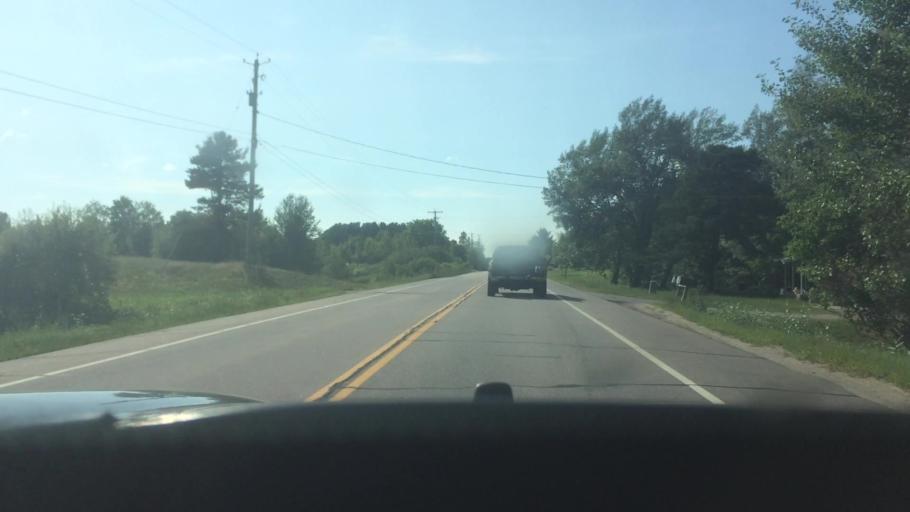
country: US
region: New York
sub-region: Franklin County
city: Malone
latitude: 44.8548
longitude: -74.2207
